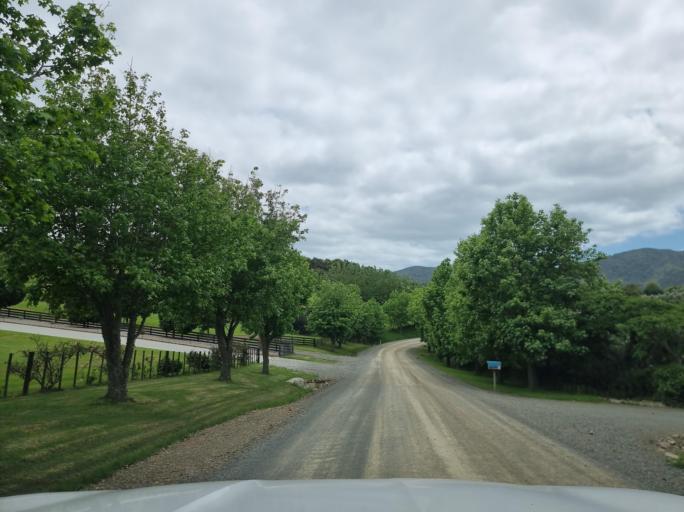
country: NZ
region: Auckland
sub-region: Auckland
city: Wellsford
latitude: -36.0930
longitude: 174.5293
